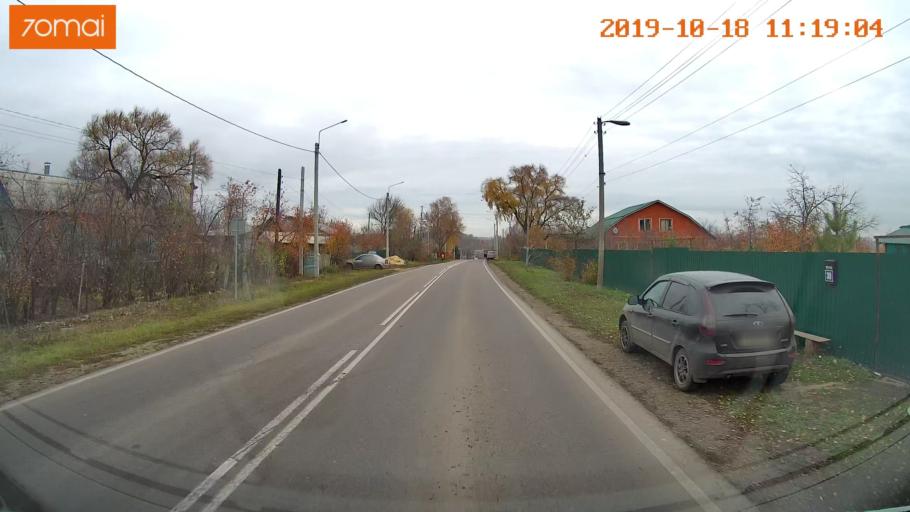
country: RU
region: Tula
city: Kimovsk
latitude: 54.0424
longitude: 38.5515
